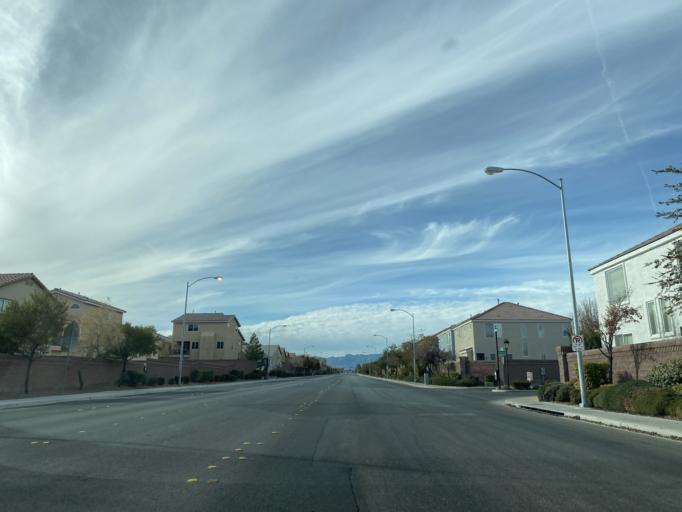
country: US
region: Nevada
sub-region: Clark County
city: Enterprise
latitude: 36.0349
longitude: -115.2273
